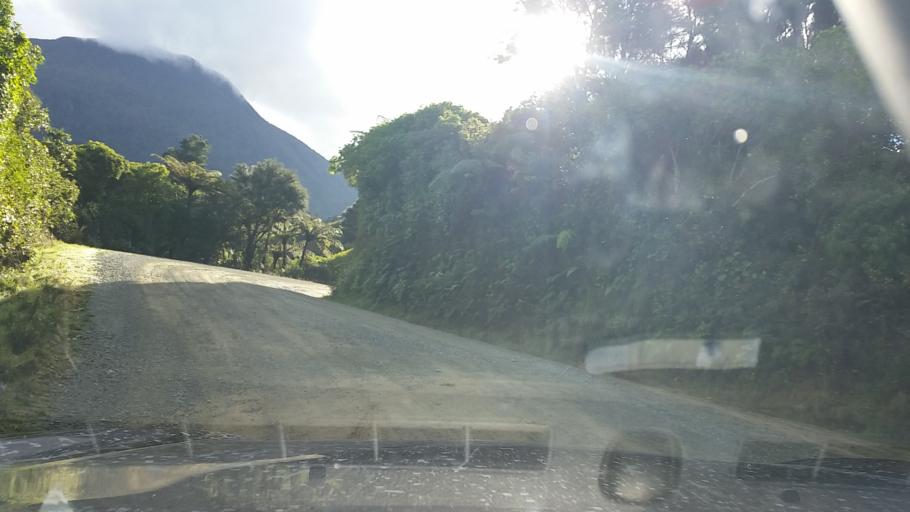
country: NZ
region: Marlborough
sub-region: Marlborough District
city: Picton
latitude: -41.1295
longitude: 174.1425
